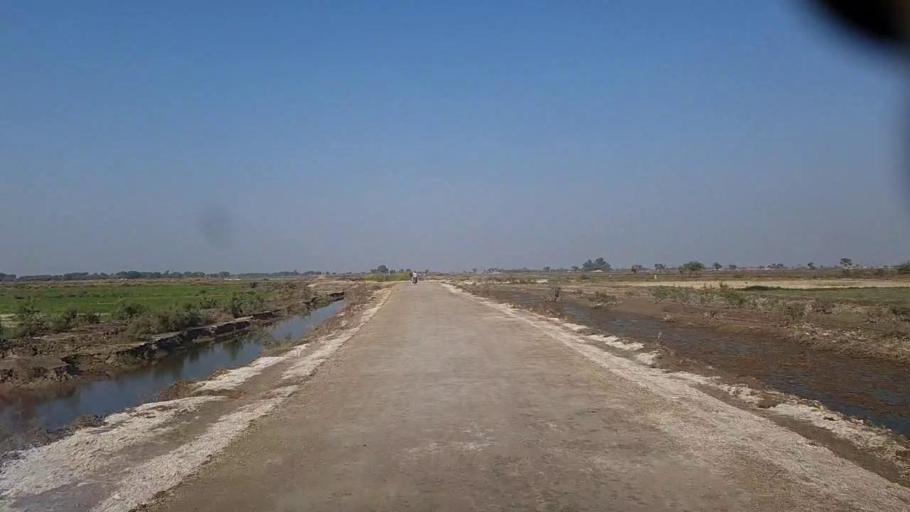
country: PK
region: Sindh
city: Jacobabad
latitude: 28.3082
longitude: 68.5614
